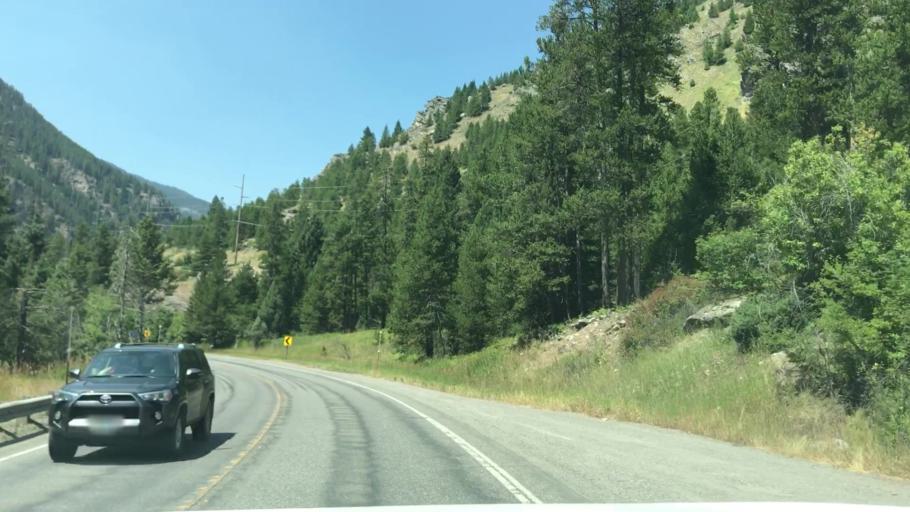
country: US
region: Montana
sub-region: Gallatin County
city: Big Sky
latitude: 45.3900
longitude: -111.1987
